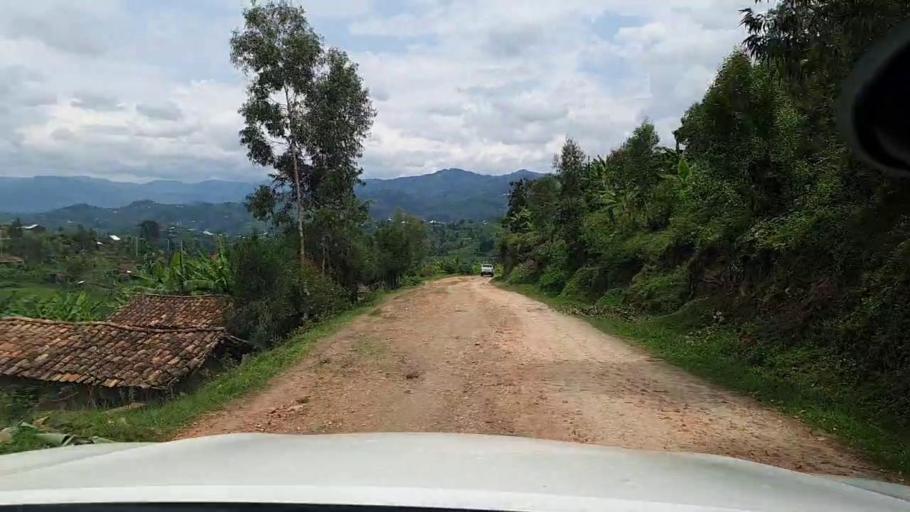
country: RW
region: Western Province
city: Kibuye
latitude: -2.0826
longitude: 29.4179
